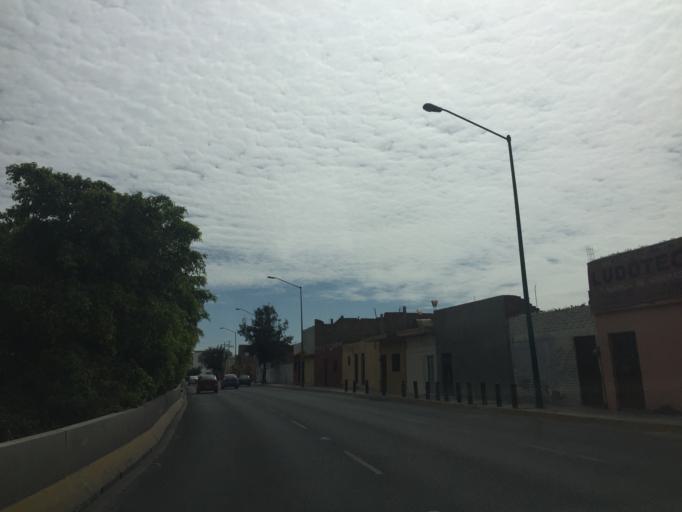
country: MX
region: Guanajuato
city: Leon
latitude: 21.1199
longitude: -101.6712
